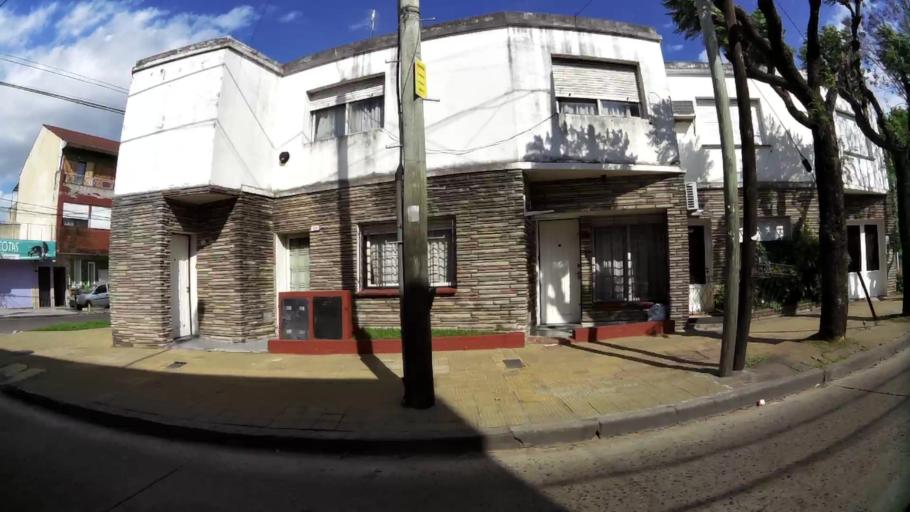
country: AR
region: Buenos Aires
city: San Justo
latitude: -34.6536
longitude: -58.5775
